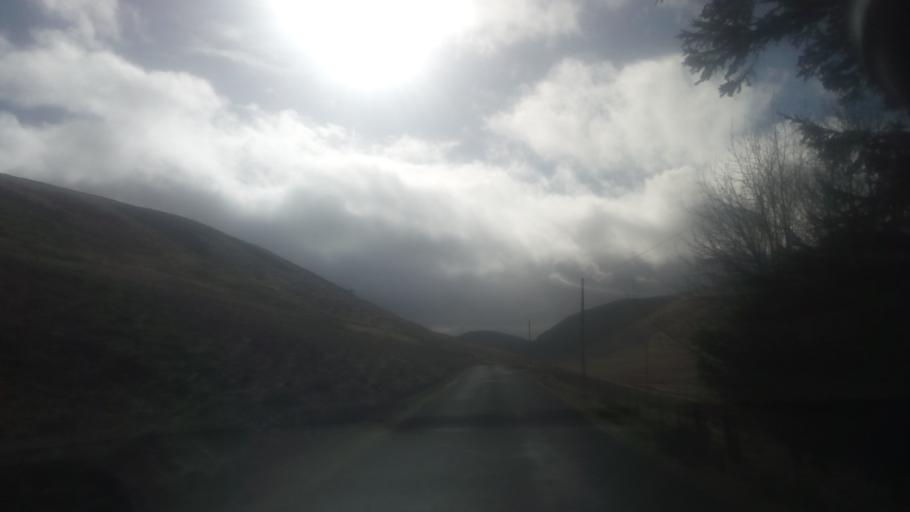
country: GB
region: Scotland
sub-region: The Scottish Borders
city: Innerleithen
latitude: 55.4922
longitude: -3.1217
